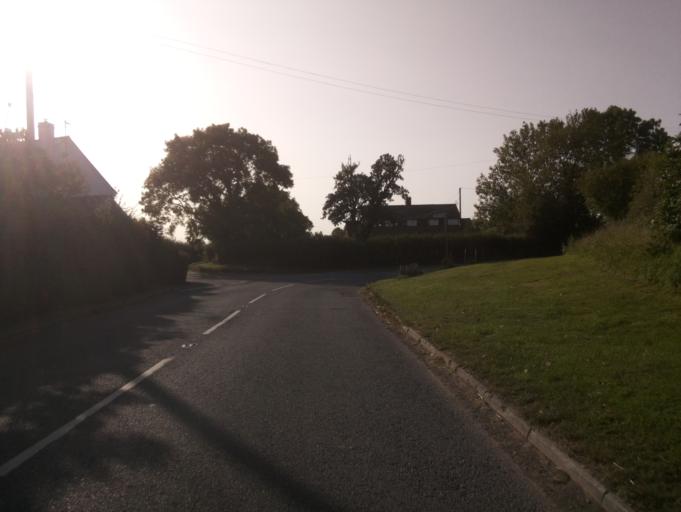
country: GB
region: England
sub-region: Gloucestershire
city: Newent
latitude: 51.9665
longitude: -2.3036
